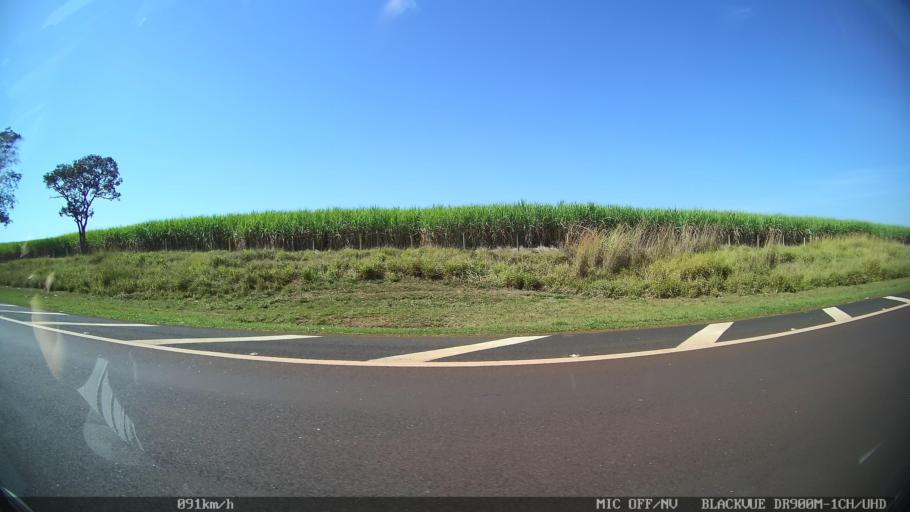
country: BR
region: Sao Paulo
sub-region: Batatais
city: Batatais
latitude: -20.8345
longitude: -47.6007
